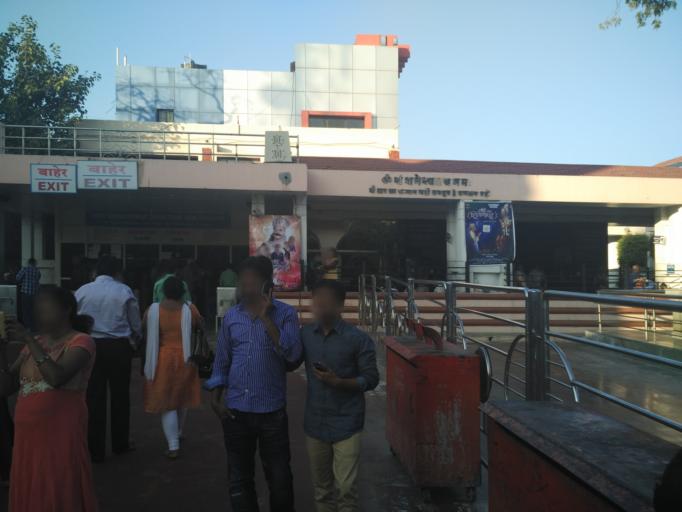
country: IN
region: Maharashtra
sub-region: Ahmadnagar
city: Rahuri
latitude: 19.3819
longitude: 74.8578
